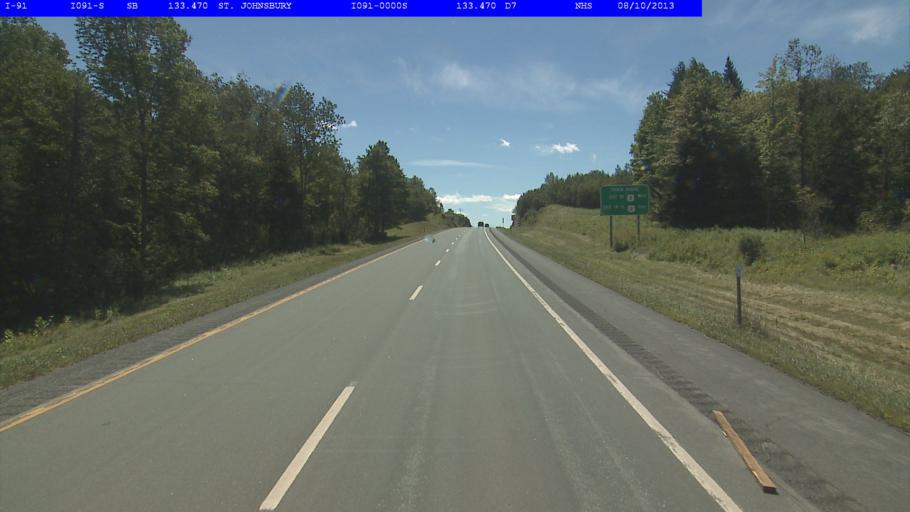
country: US
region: Vermont
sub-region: Caledonia County
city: St Johnsbury
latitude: 44.4672
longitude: -72.0248
